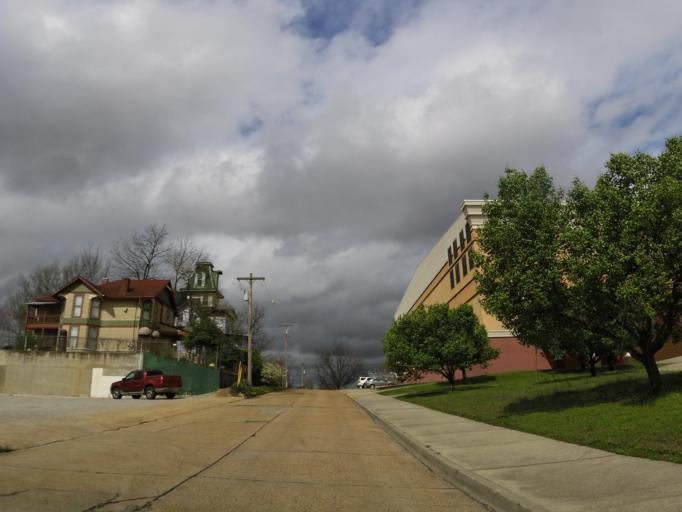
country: US
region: Missouri
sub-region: Butler County
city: Poplar Bluff
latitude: 36.7539
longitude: -90.3965
